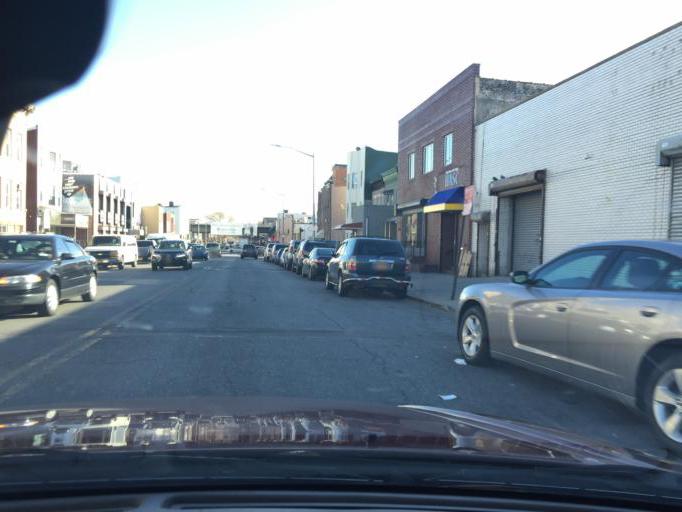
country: US
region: New York
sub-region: Kings County
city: Bensonhurst
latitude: 40.6286
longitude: -73.9983
